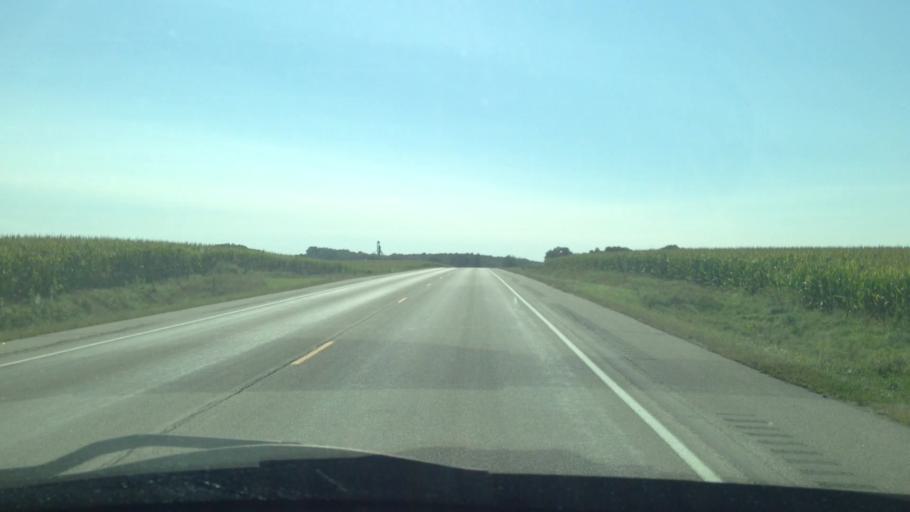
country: US
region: Minnesota
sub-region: Winona County
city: Lewiston
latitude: 43.9813
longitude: -91.9469
